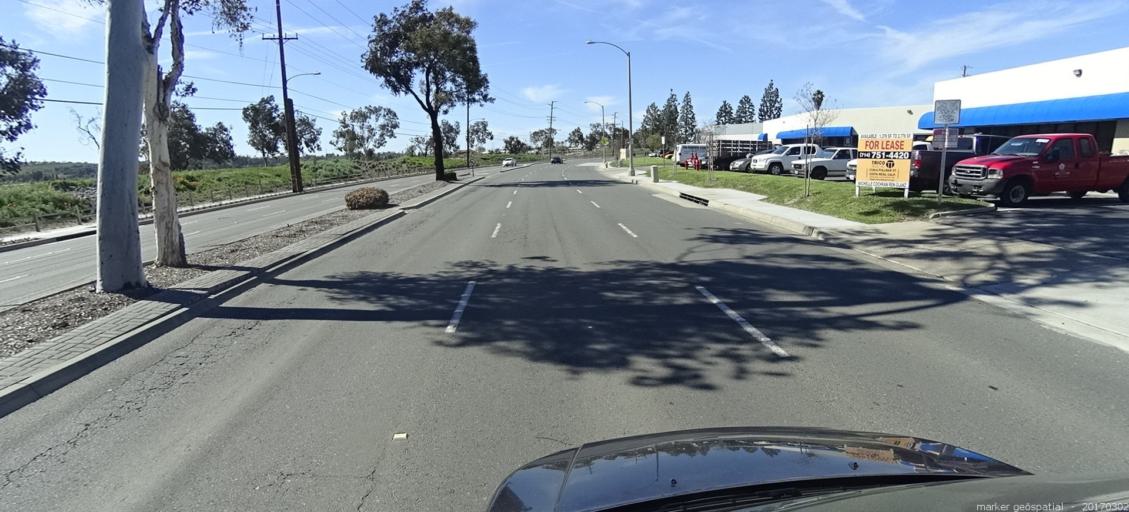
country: US
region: California
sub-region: Orange County
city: Yorba Linda
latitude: 33.8570
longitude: -117.8324
